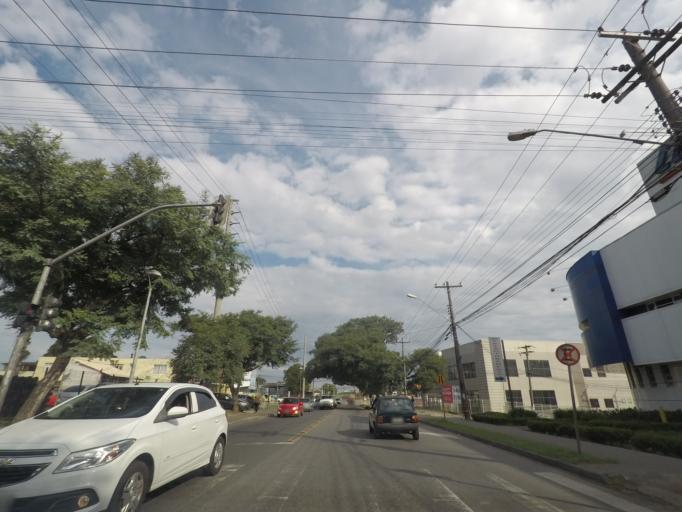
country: BR
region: Parana
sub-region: Sao Jose Dos Pinhais
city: Sao Jose dos Pinhais
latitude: -25.5411
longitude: -49.2945
